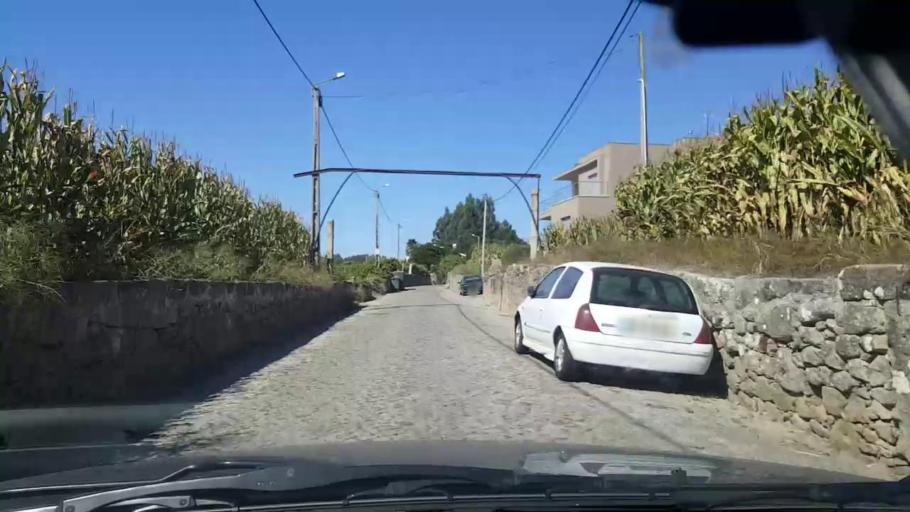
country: PT
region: Porto
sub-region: Vila do Conde
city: Arvore
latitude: 41.3136
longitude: -8.6728
